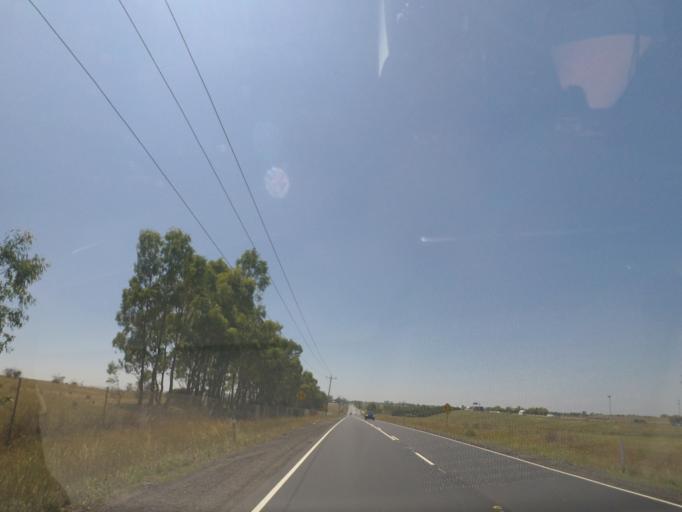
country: AU
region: Victoria
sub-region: Hume
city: Craigieburn
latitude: -37.6022
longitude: 144.9698
